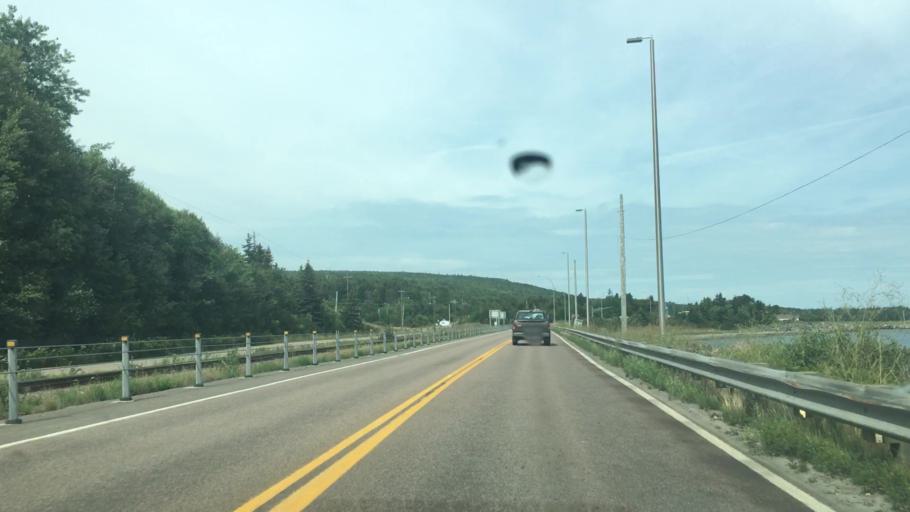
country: CA
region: Nova Scotia
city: Port Hawkesbury
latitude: 45.6435
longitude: -61.4321
